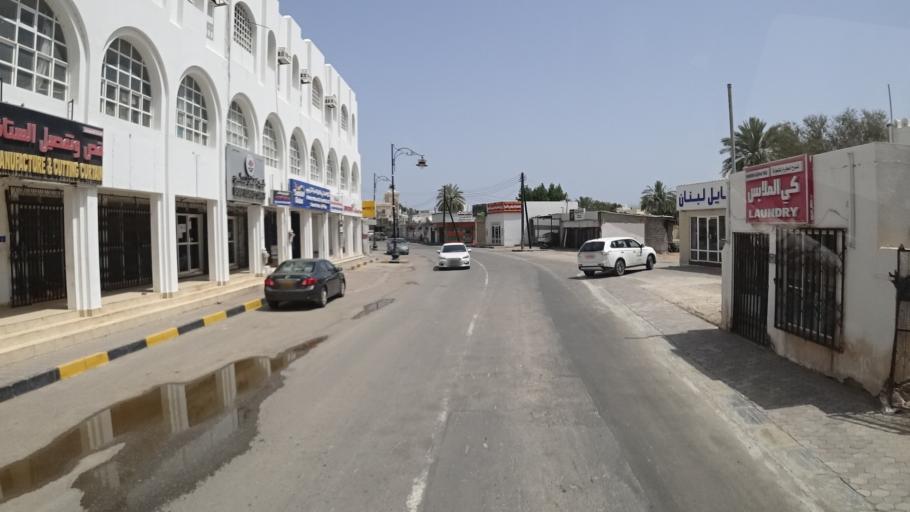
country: OM
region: Muhafazat Masqat
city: Muscat
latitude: 23.2603
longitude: 58.9152
